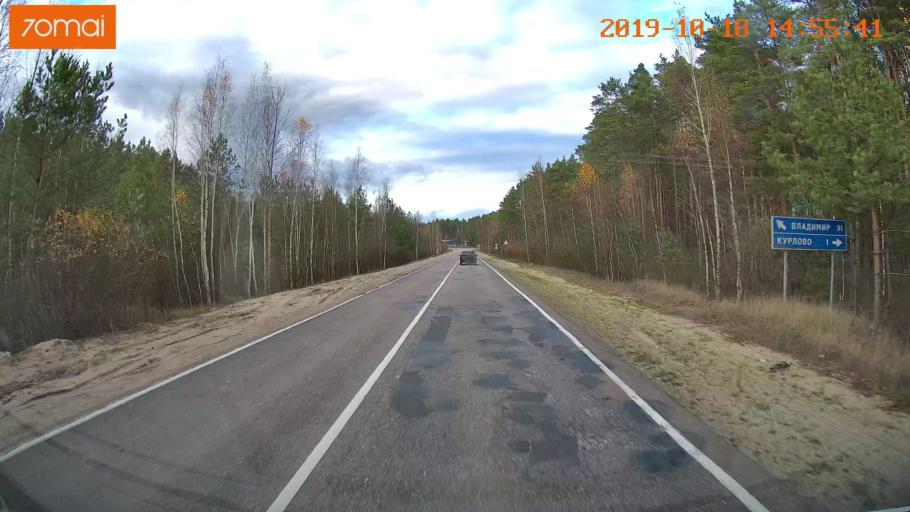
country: RU
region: Vladimir
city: Kurlovo
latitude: 55.4557
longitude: 40.5894
